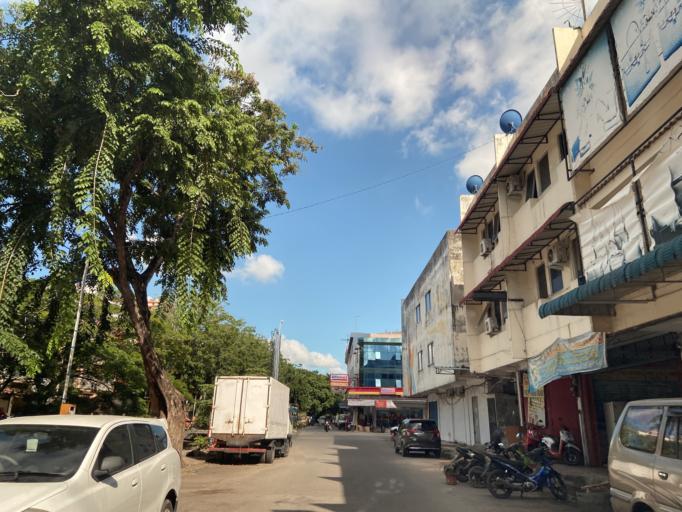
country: SG
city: Singapore
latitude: 1.1453
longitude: 104.0075
